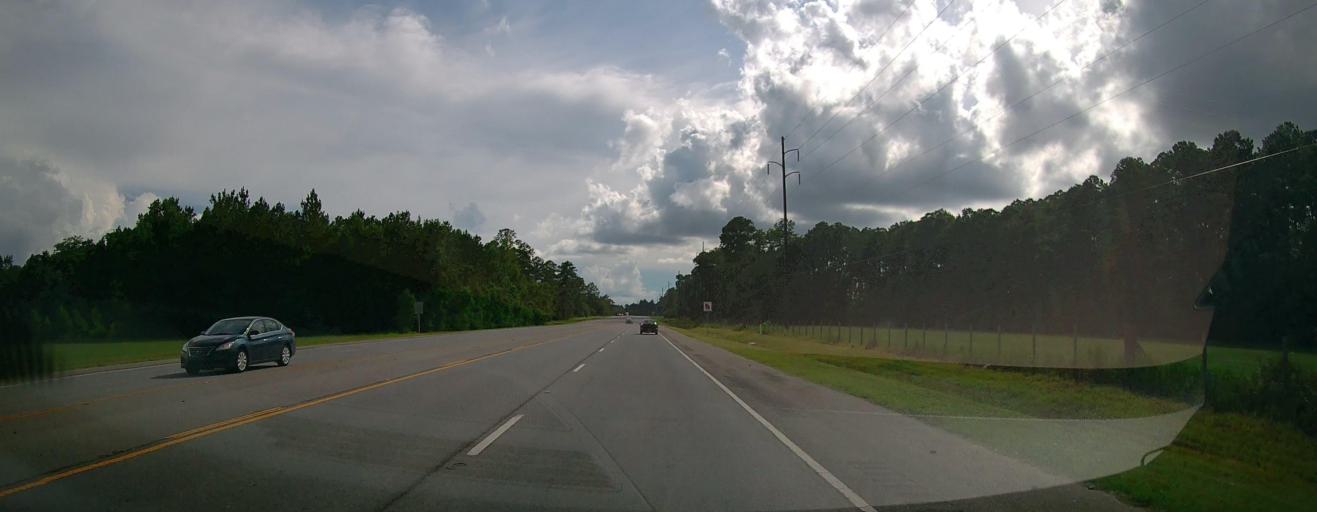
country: US
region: Georgia
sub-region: Wayne County
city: Jesup
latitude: 31.5962
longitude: -81.9402
